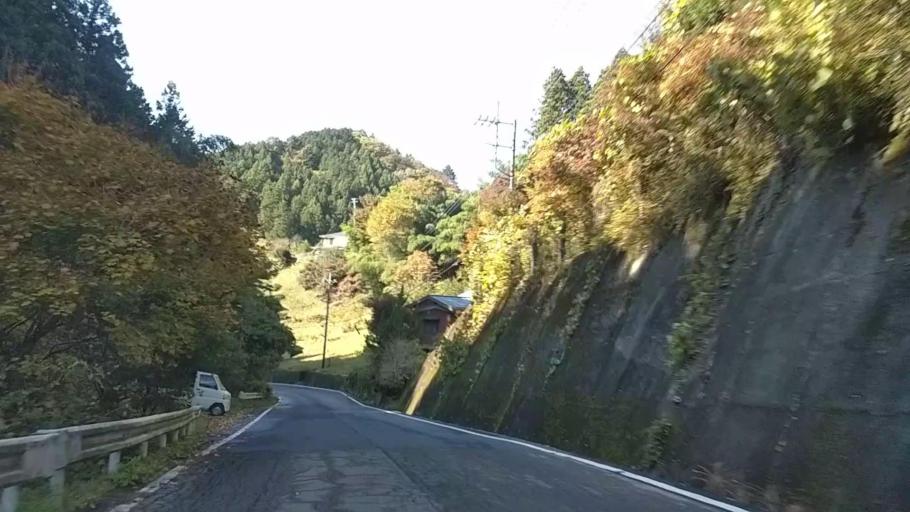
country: JP
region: Yamanashi
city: Uenohara
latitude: 35.6994
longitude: 139.0293
